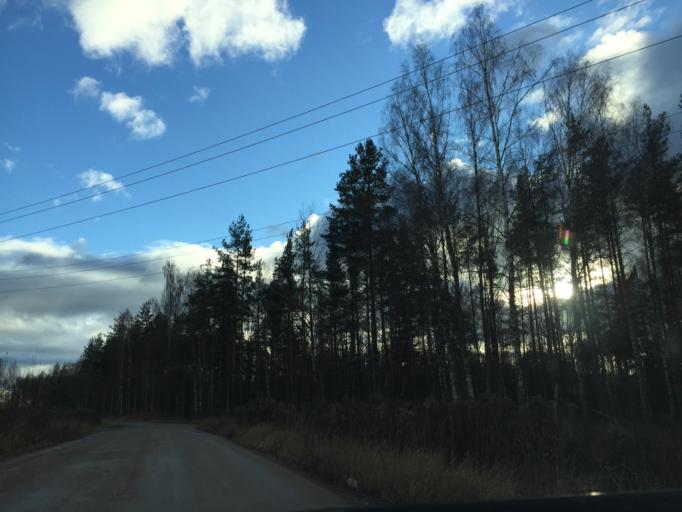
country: LV
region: Koceni
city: Koceni
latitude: 57.5387
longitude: 25.3777
